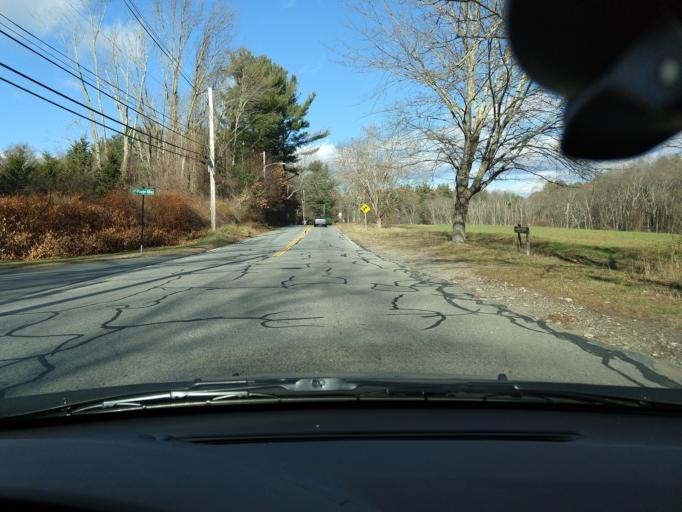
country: US
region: Massachusetts
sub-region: Middlesex County
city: West Concord
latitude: 42.4293
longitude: -71.3757
